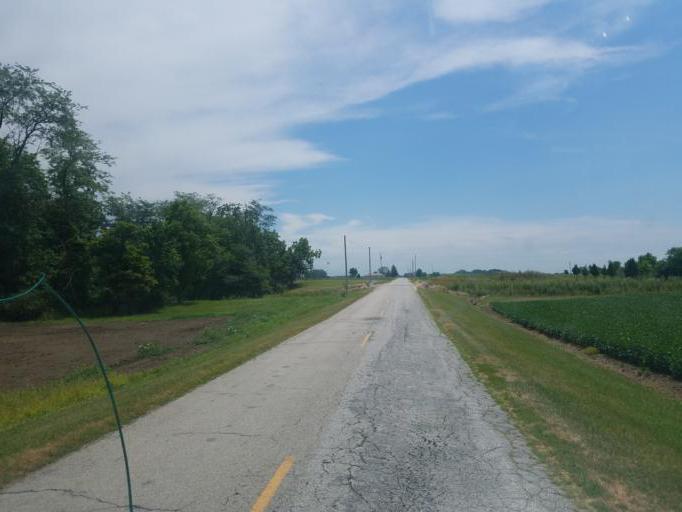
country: US
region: Ohio
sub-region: Paulding County
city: Antwerp
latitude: 41.2282
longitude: -84.7277
